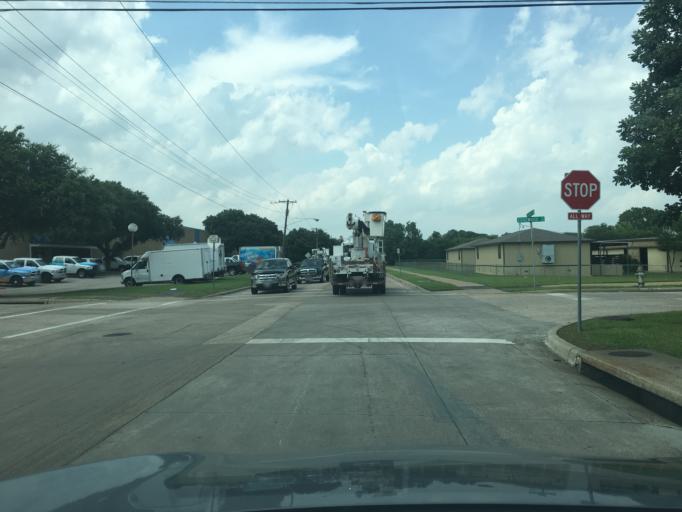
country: US
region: Texas
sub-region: Dallas County
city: Garland
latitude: 32.9138
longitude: -96.6768
